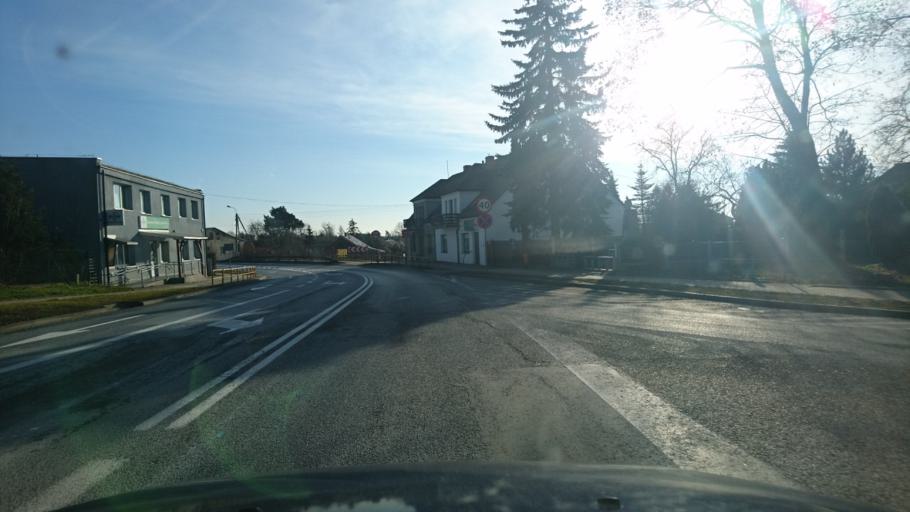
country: PL
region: Opole Voivodeship
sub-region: Powiat oleski
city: Dalachow
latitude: 51.0389
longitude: 18.5981
